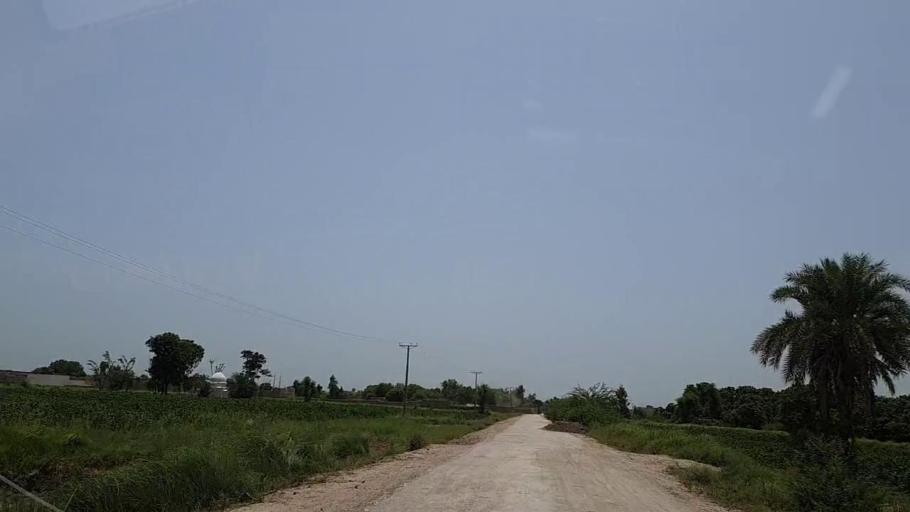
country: PK
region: Sindh
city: Tharu Shah
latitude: 26.9431
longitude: 68.1068
